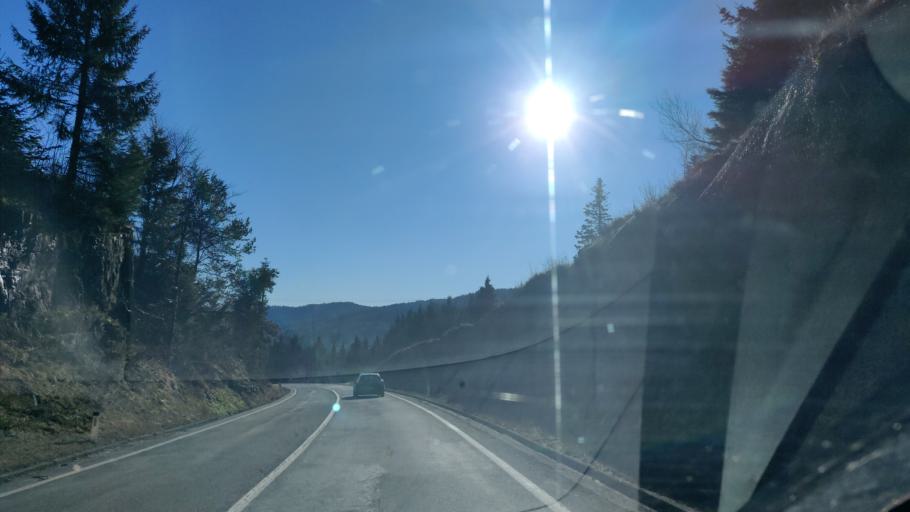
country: SI
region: Logatec
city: Logatec
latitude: 45.8830
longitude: 14.2036
